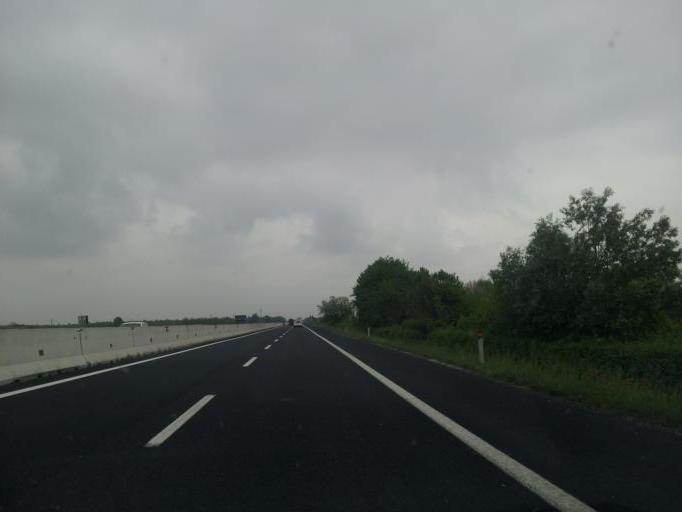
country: IT
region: Veneto
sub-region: Provincia di Venezia
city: Santo Stino di Livenza
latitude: 45.7405
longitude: 12.6916
